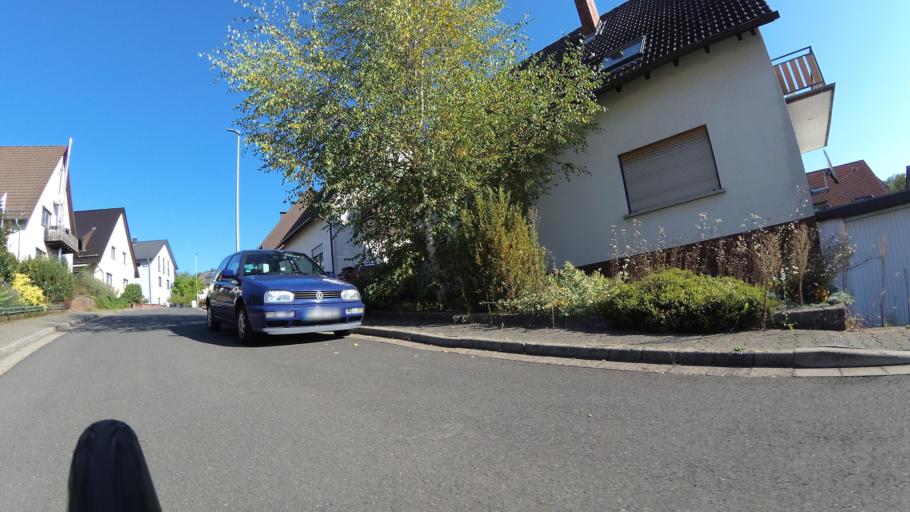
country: DE
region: Rheinland-Pfalz
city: Waldmohr
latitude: 49.3932
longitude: 7.3309
